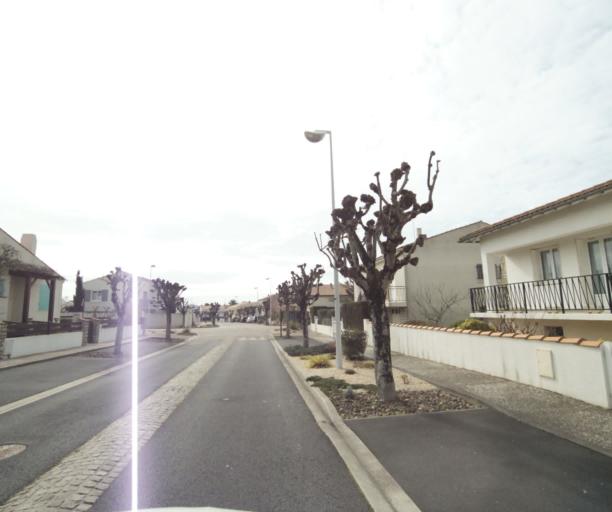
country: FR
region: Poitou-Charentes
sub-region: Departement de la Charente-Maritime
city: Lagord
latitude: 46.1879
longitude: -1.1578
